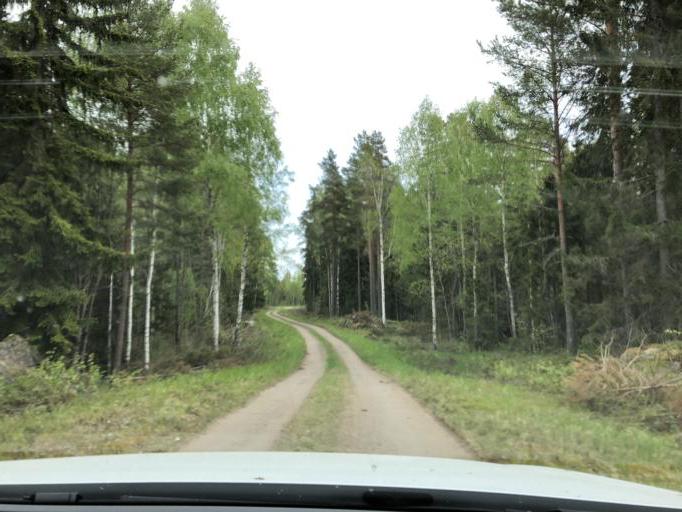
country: SE
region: Uppsala
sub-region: Heby Kommun
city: OEstervala
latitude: 60.3738
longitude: 17.2369
